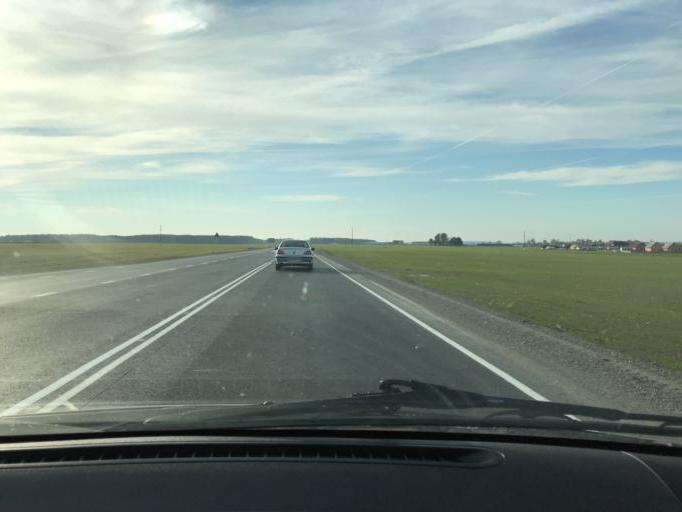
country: BY
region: Brest
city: Horad Pinsk
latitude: 52.1686
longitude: 26.0176
